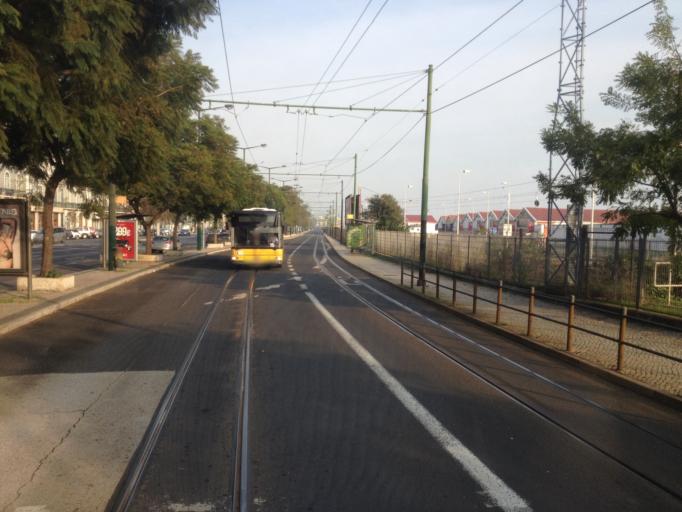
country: PT
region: Setubal
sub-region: Almada
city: Cacilhas
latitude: 38.7064
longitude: -9.1547
